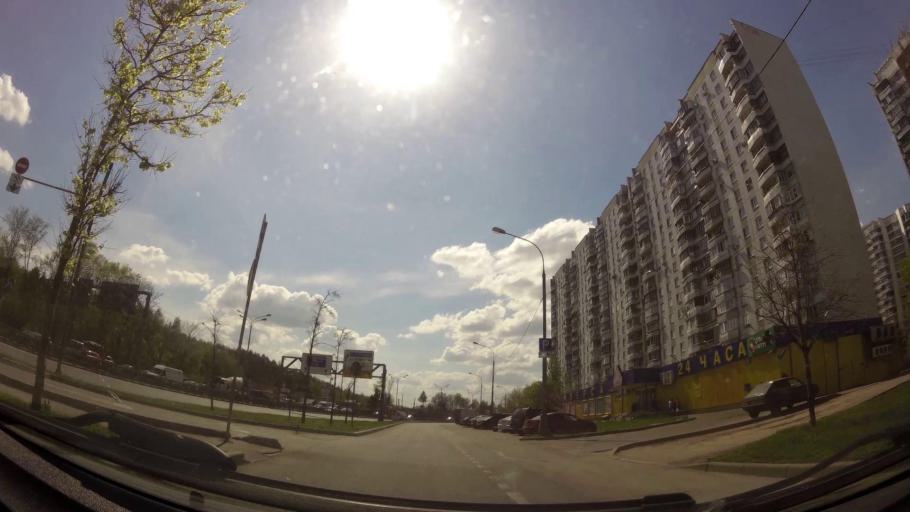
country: RU
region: Moscow
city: Novo-Peredelkino
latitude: 55.6353
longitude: 37.3467
